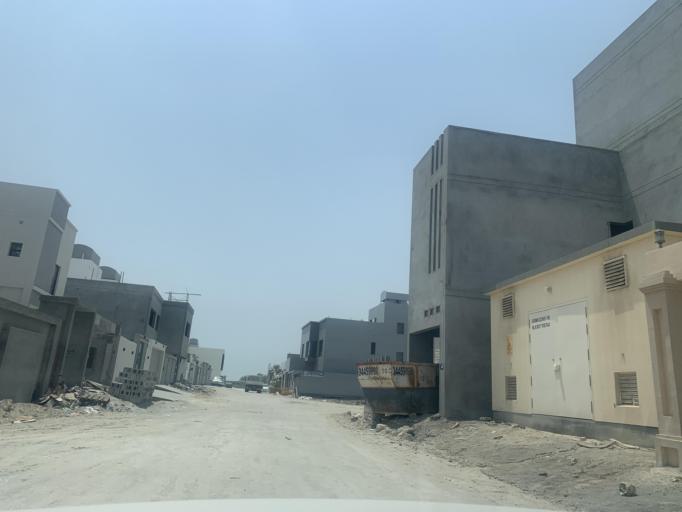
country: BH
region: Central Governorate
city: Madinat Hamad
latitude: 26.1314
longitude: 50.4664
